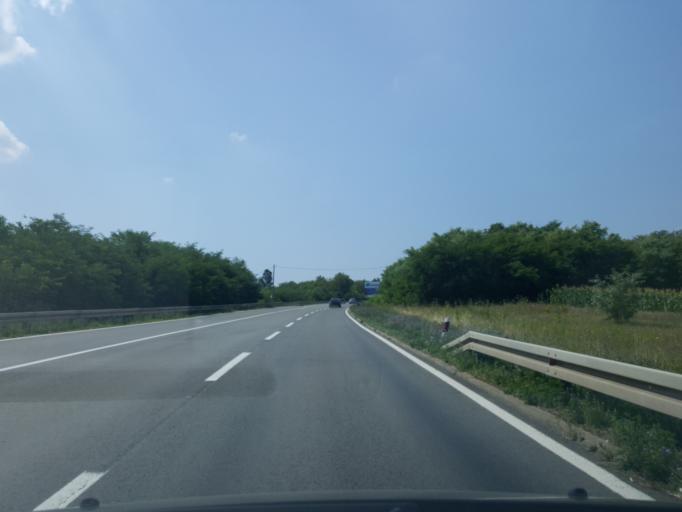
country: RS
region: Central Serbia
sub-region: Belgrade
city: Sopot
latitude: 44.5549
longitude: 20.6667
